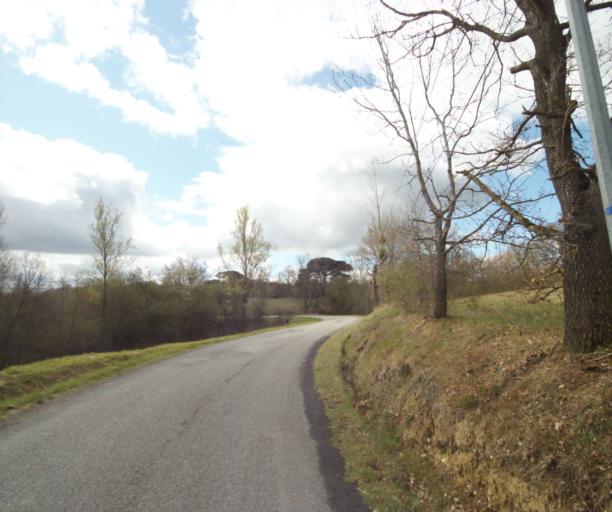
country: FR
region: Midi-Pyrenees
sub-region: Departement de l'Ariege
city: Saverdun
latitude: 43.2059
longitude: 1.5752
